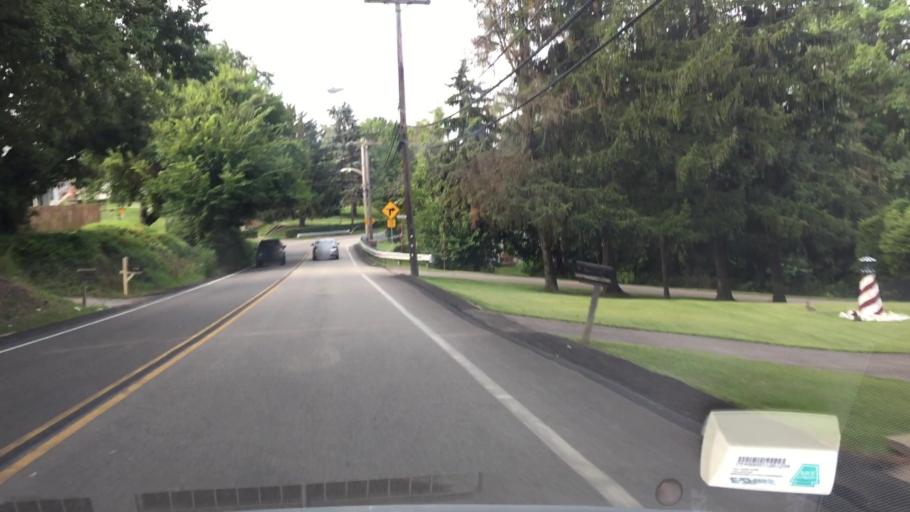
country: US
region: Pennsylvania
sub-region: Allegheny County
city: Ben Avon
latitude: 40.4797
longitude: -80.0924
